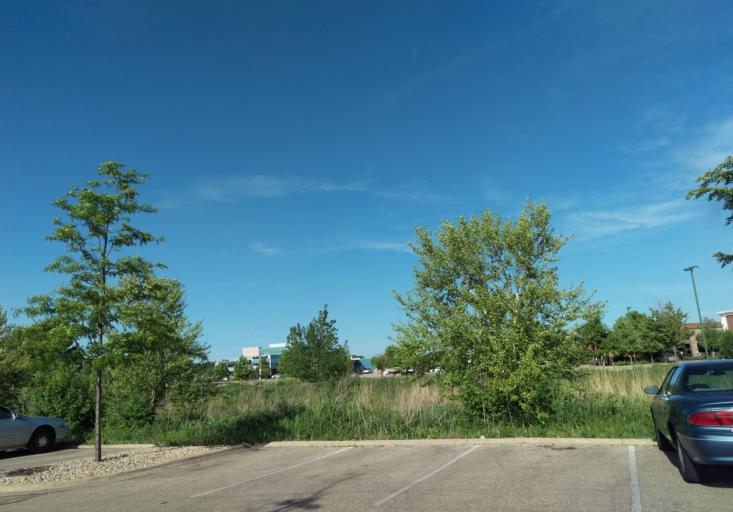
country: US
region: Wisconsin
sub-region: Dane County
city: Middleton
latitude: 43.0977
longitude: -89.5218
